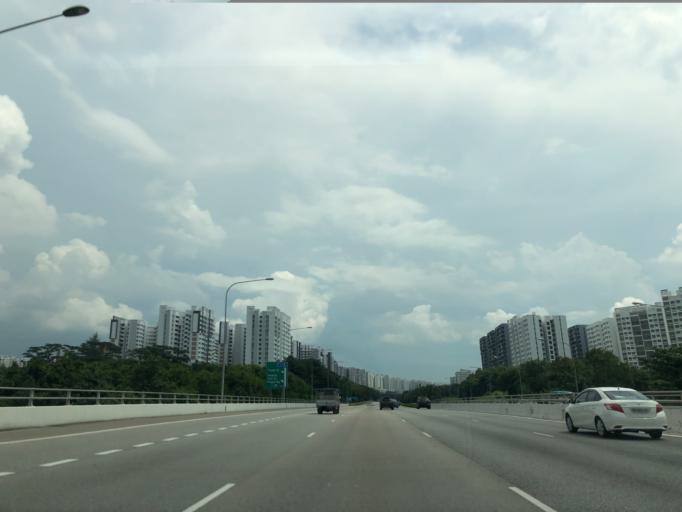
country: MY
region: Johor
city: Kampung Pasir Gudang Baru
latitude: 1.4013
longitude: 103.8864
